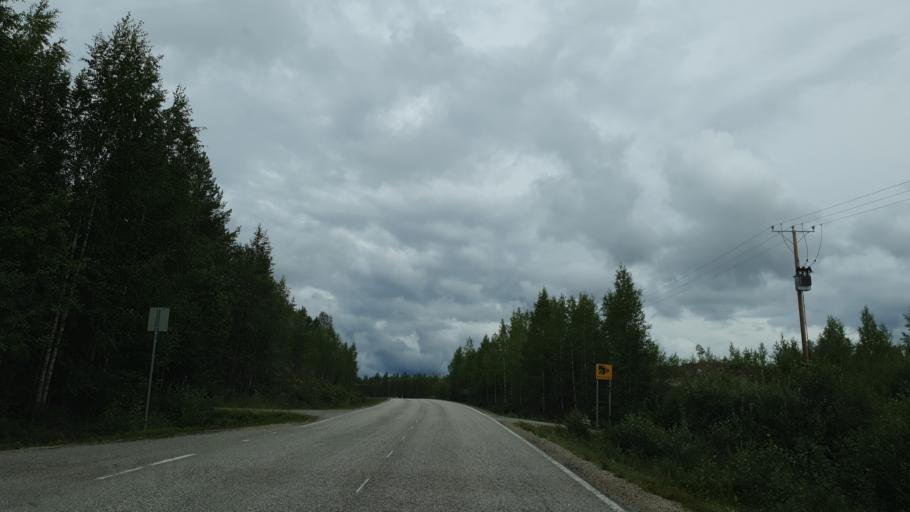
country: FI
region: Kainuu
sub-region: Kehys-Kainuu
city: Kuhmo
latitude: 64.2303
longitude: 29.8186
